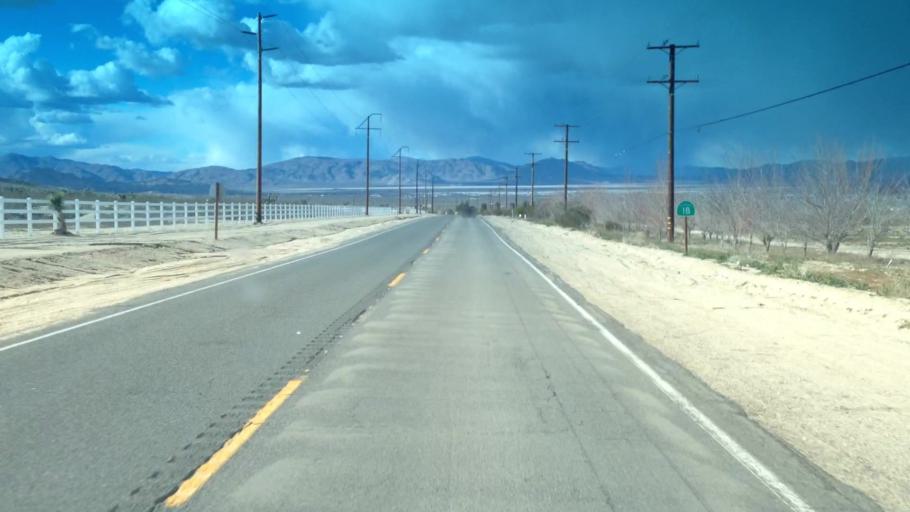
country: US
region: California
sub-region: San Bernardino County
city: Lucerne Valley
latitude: 34.3968
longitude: -116.8872
